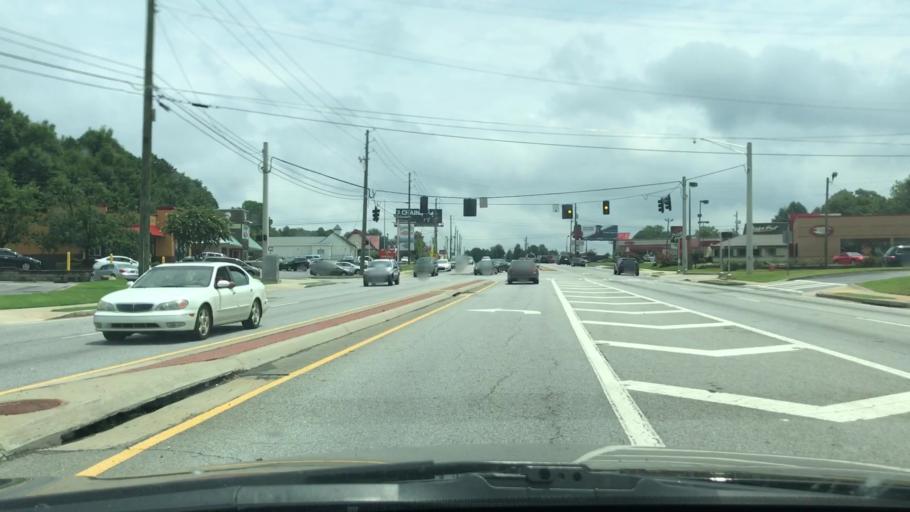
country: US
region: Georgia
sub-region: Gwinnett County
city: Lilburn
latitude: 33.9035
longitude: -84.1193
